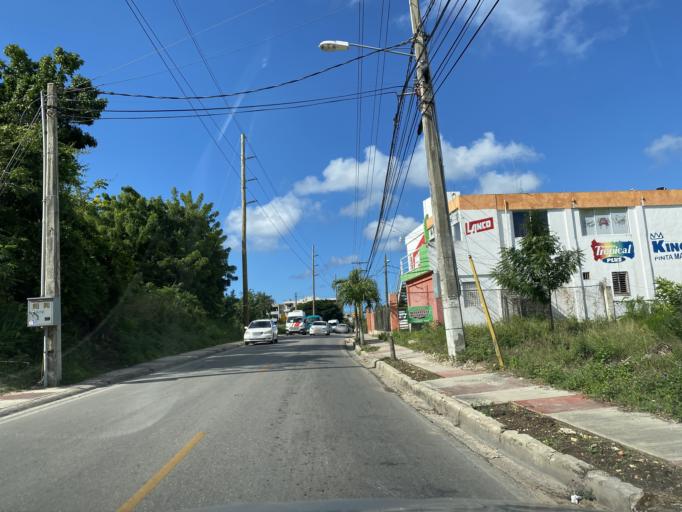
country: DO
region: La Romana
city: La Romana
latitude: 18.3705
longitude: -68.8335
